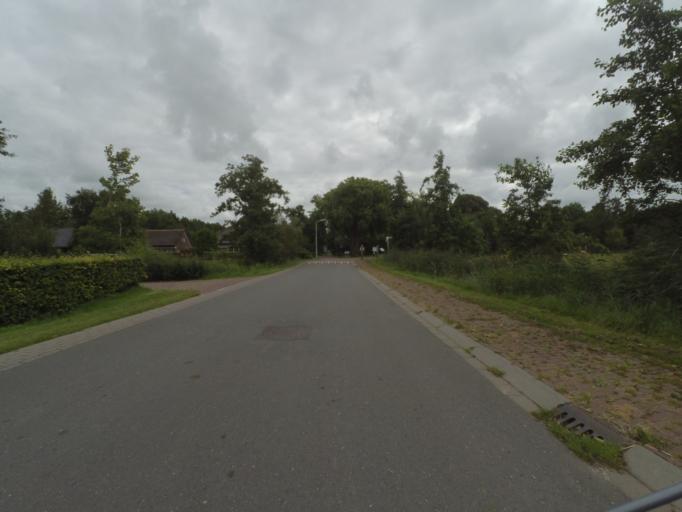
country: NL
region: Friesland
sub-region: Gemeente Kollumerland en Nieuwkruisland
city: Kollumerzwaag
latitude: 53.2940
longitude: 6.0862
